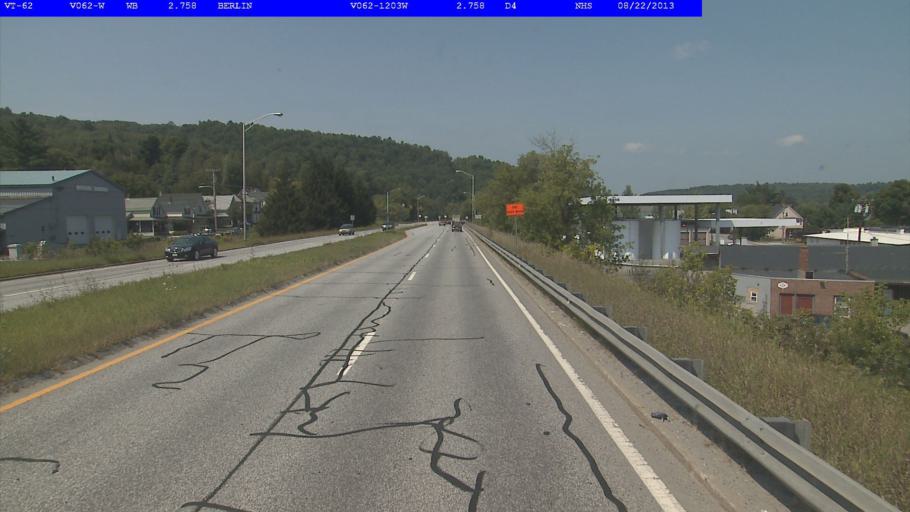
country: US
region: Vermont
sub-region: Washington County
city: Barre
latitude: 44.2033
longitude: -72.5124
